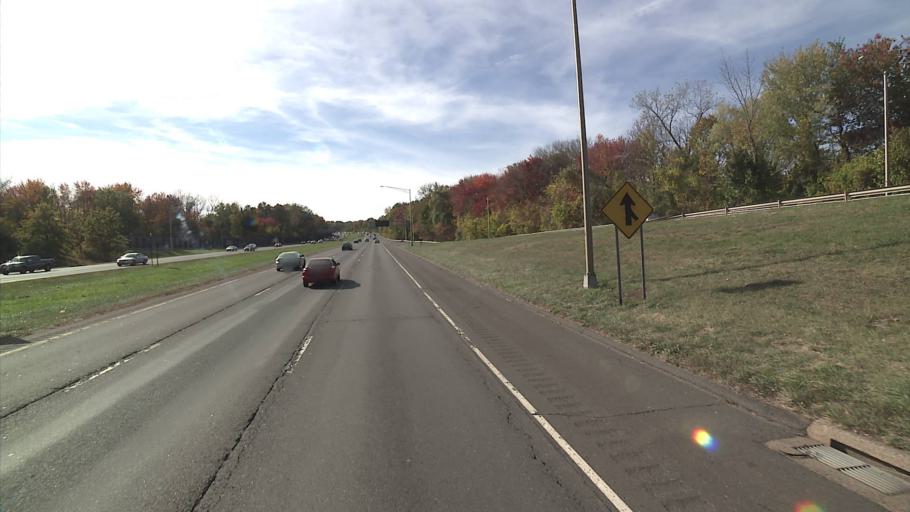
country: US
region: Connecticut
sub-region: Hartford County
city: West Hartford
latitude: 41.7353
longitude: -72.7440
